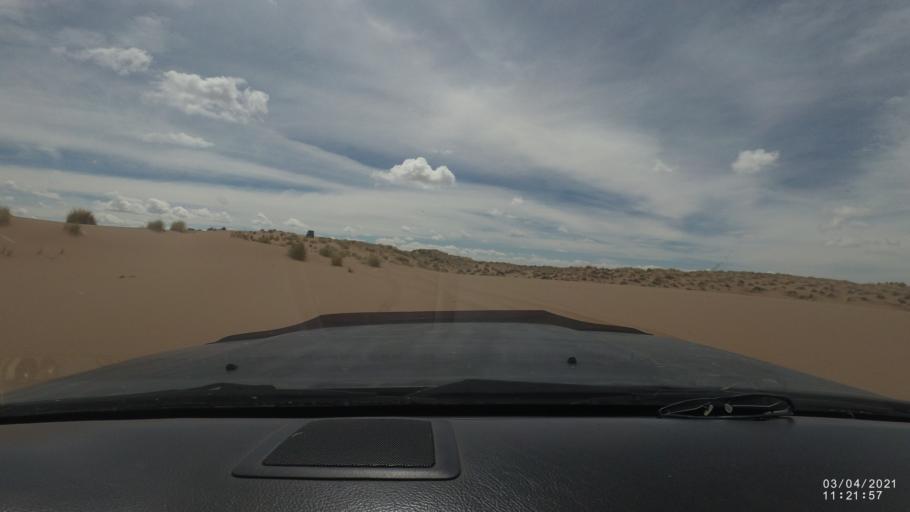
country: BO
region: Oruro
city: Poopo
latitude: -18.7043
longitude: -67.5130
